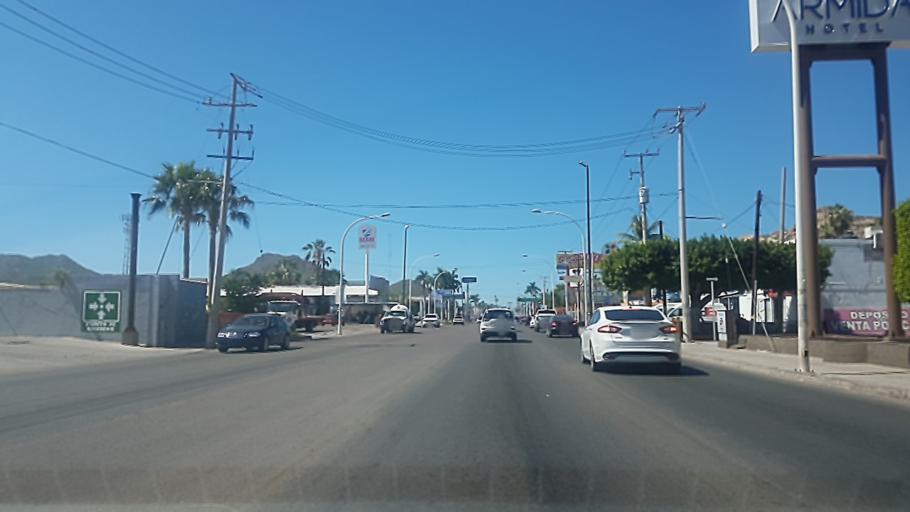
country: MX
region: Sonora
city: Heroica Guaymas
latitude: 27.9249
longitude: -110.9078
